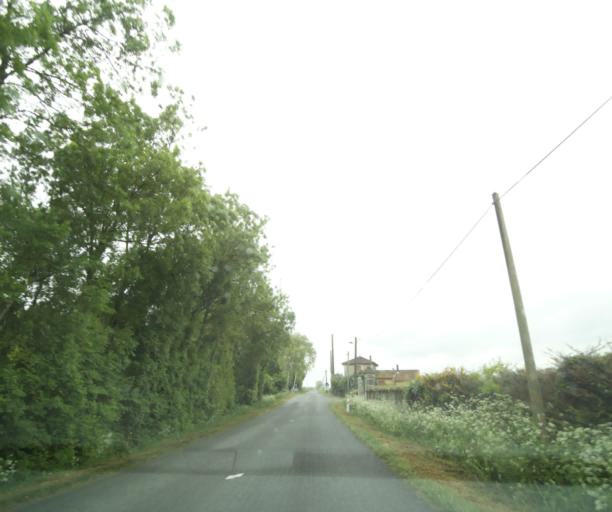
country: FR
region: Poitou-Charentes
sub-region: Departement de la Charente-Maritime
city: Pons
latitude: 45.6480
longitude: -0.5350
